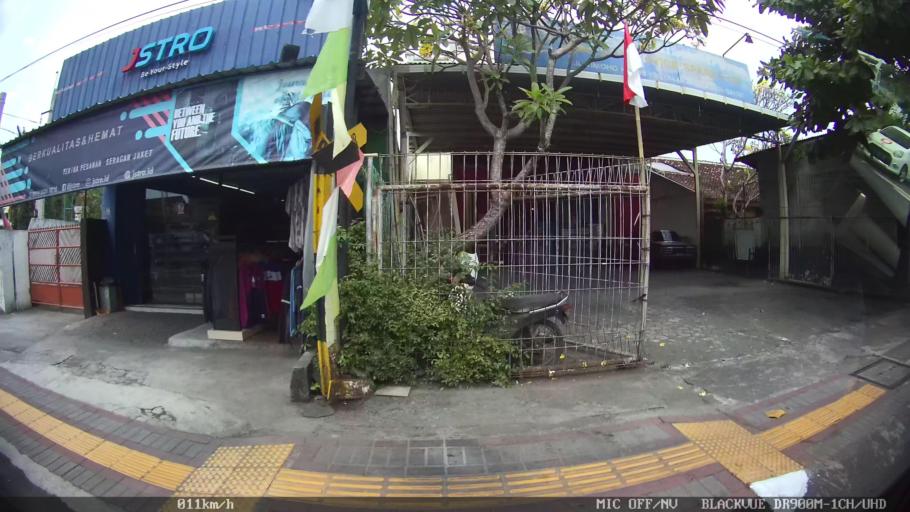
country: ID
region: Daerah Istimewa Yogyakarta
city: Yogyakarta
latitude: -7.7887
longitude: 110.3936
